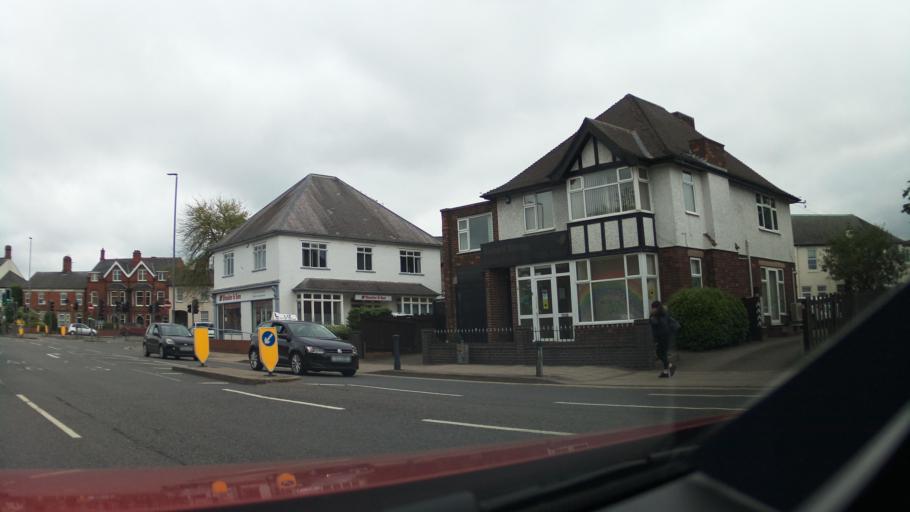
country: GB
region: England
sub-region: Leicestershire
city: Melton Mowbray
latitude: 52.7661
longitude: -0.8897
